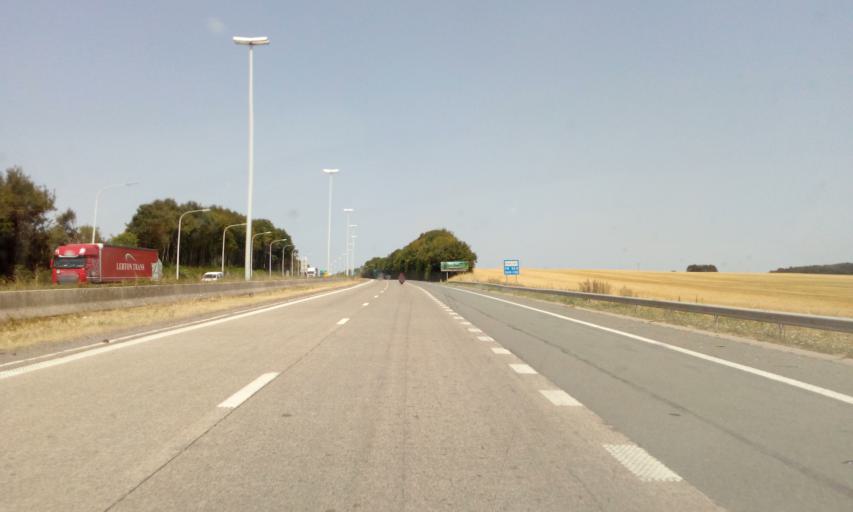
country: BE
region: Wallonia
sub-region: Province de Namur
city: Assesse
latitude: 50.3217
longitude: 5.0210
